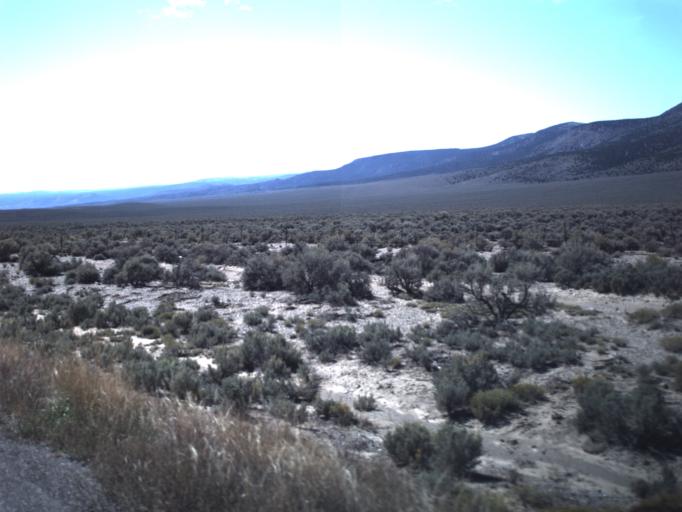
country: US
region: Utah
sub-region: Piute County
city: Junction
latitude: 38.2610
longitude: -111.9863
